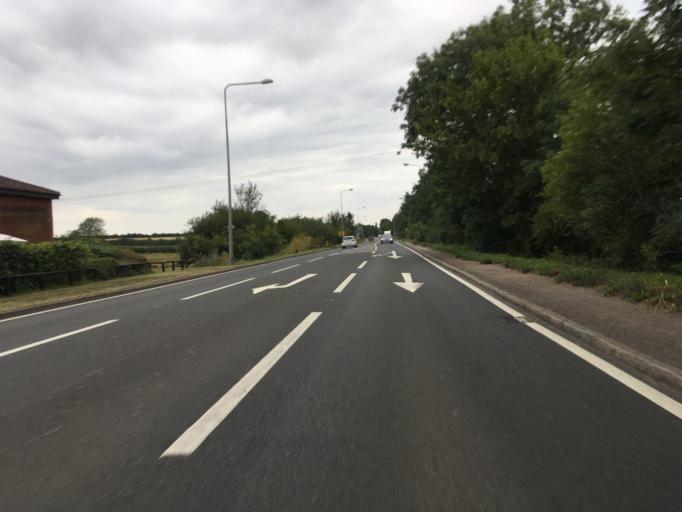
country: GB
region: England
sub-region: Central Bedfordshire
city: Hockliffe
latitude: 51.9218
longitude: -0.5723
